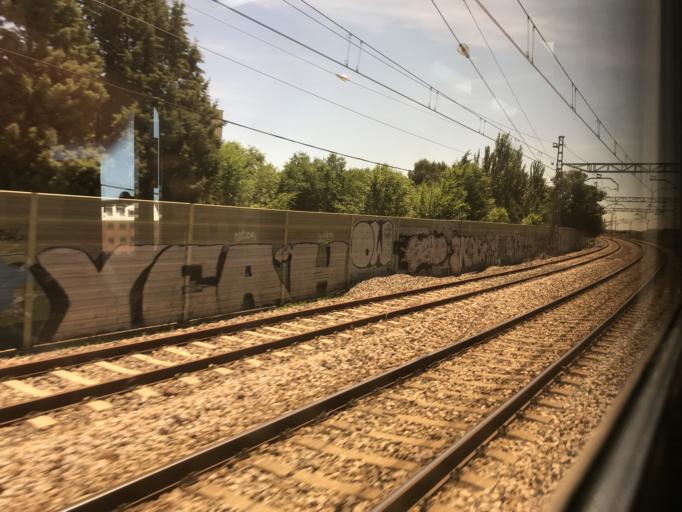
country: ES
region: Madrid
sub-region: Provincia de Madrid
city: Pinto
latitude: 40.2374
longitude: -3.7028
